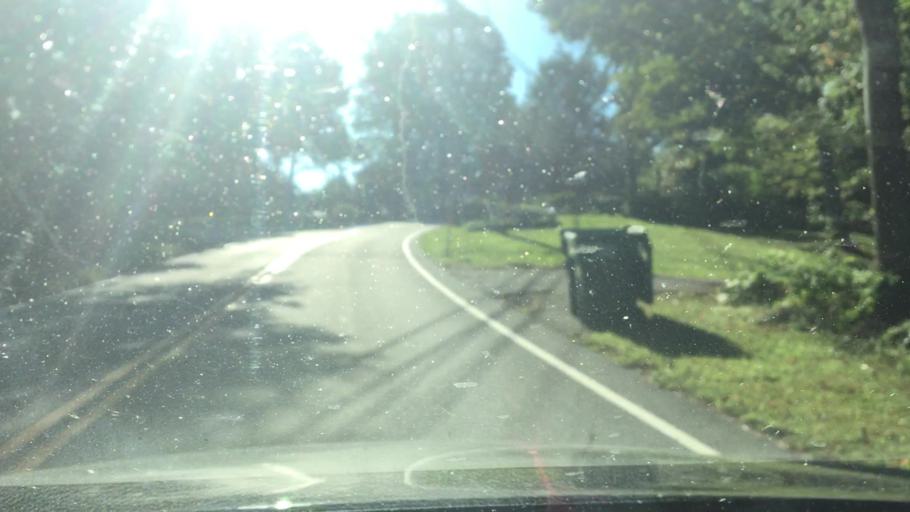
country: US
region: Connecticut
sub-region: New Haven County
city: Ansonia
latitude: 41.3696
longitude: -73.1205
